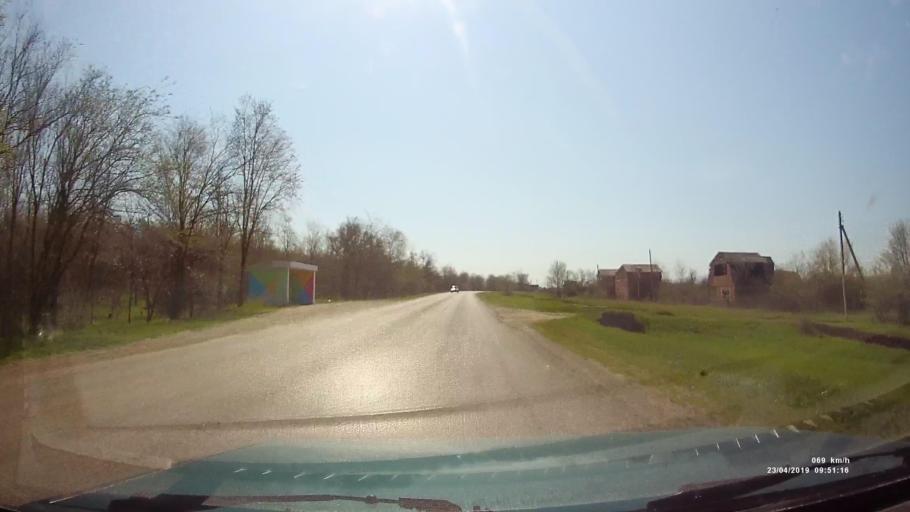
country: RU
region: Rostov
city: Orlovskiy
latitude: 46.8567
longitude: 42.0394
